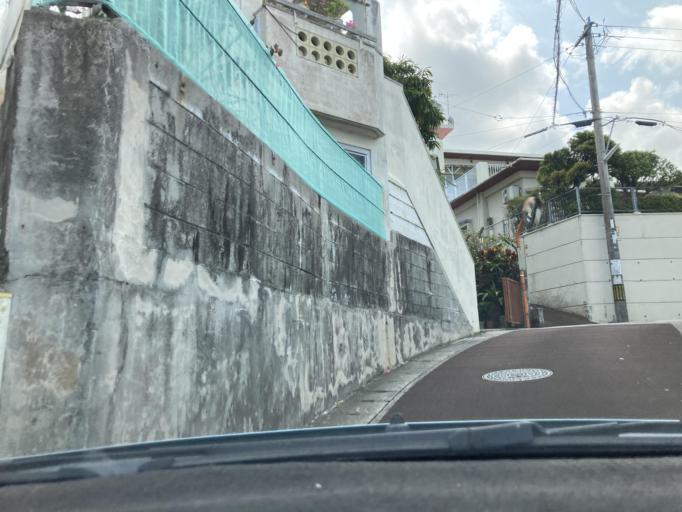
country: JP
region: Okinawa
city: Naha-shi
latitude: 26.2238
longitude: 127.7127
